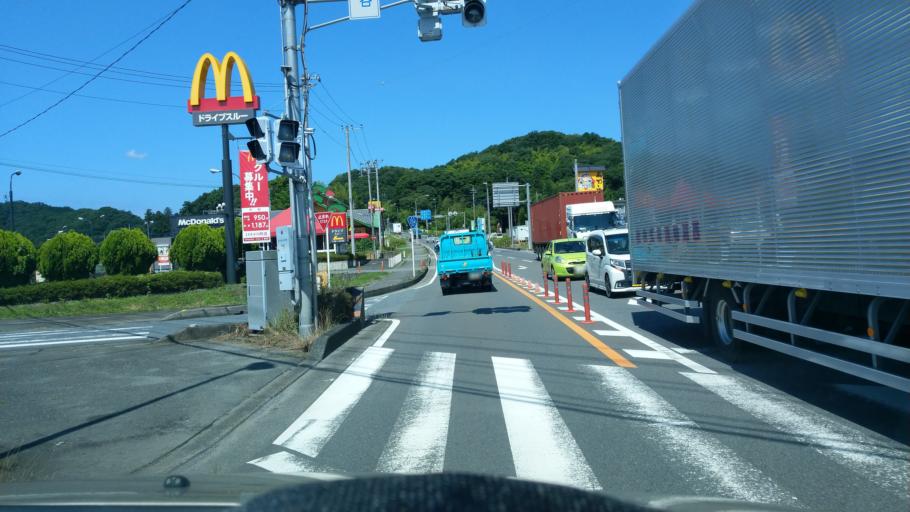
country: JP
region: Saitama
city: Ogawa
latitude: 36.0707
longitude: 139.2756
